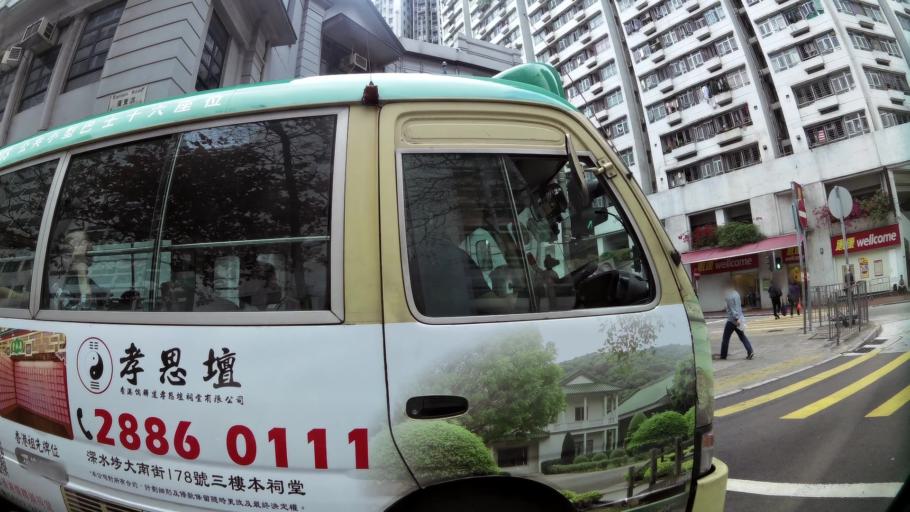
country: HK
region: Kowloon City
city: Kowloon
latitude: 22.3098
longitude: 114.1691
